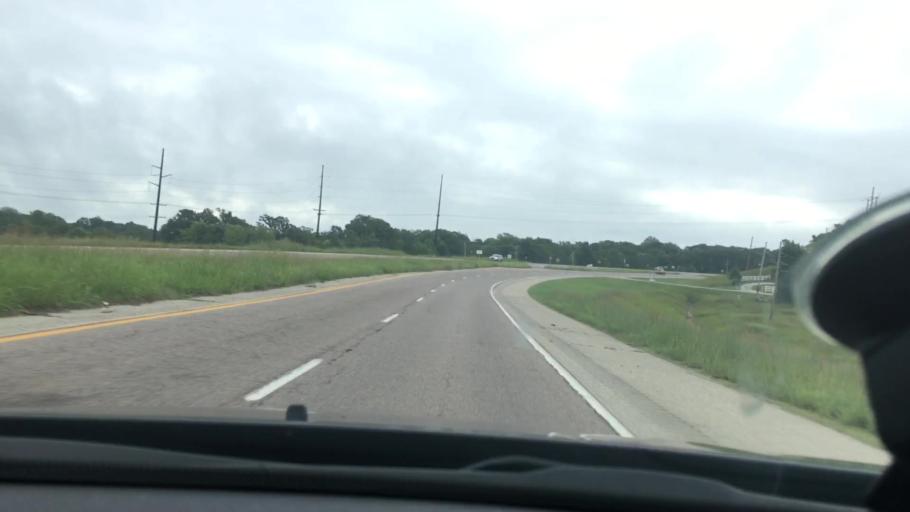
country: US
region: Oklahoma
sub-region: Pontotoc County
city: Ada
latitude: 34.7814
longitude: -96.6034
